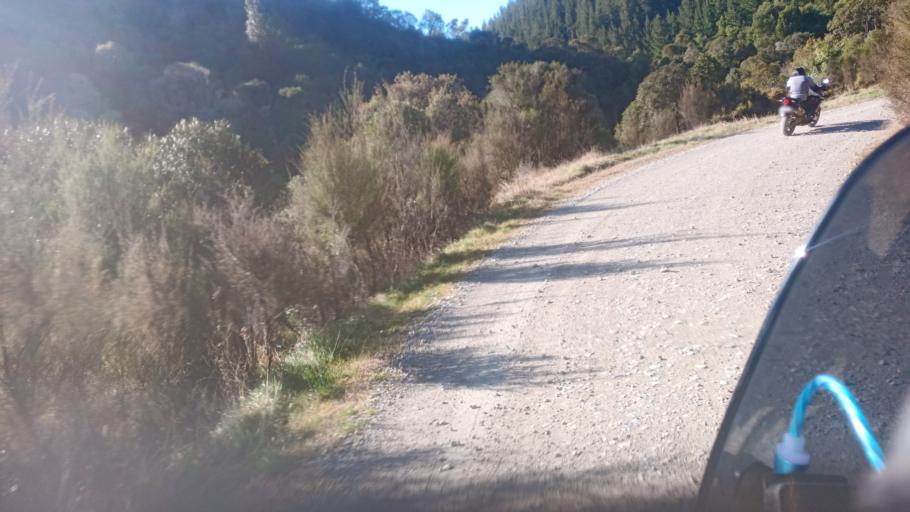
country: NZ
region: Hawke's Bay
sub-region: Wairoa District
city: Wairoa
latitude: -38.6587
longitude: 177.4976
